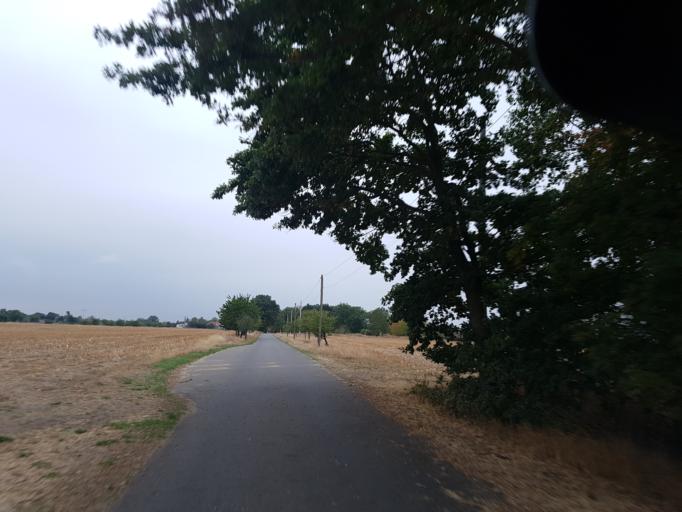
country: DE
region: Brandenburg
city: Schilda
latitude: 51.6377
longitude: 13.3238
